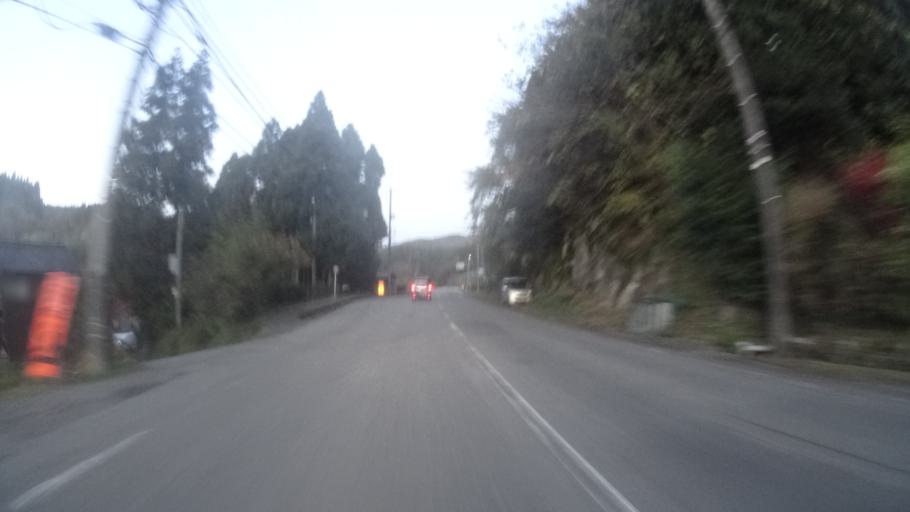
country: JP
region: Ishikawa
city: Nanao
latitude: 37.3484
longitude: 136.8608
